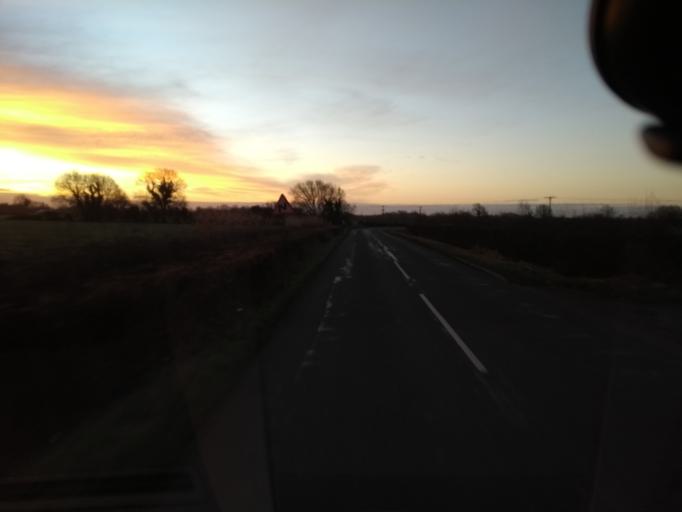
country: GB
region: England
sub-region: Somerset
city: Highbridge
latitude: 51.2286
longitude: -2.9442
